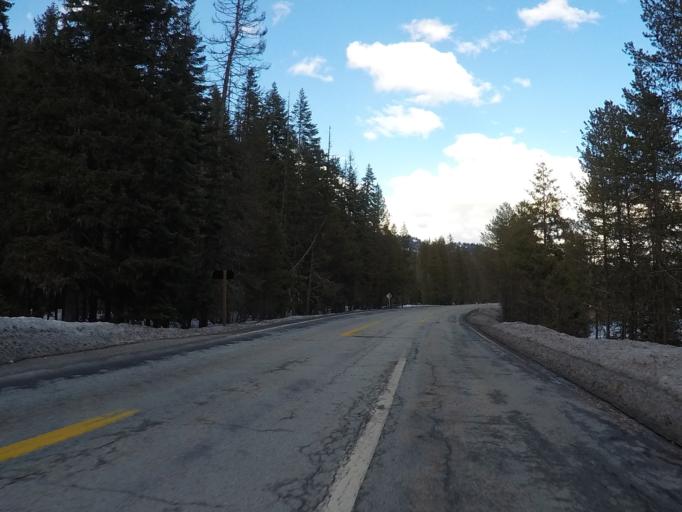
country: US
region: Montana
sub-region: Ravalli County
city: Hamilton
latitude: 46.5082
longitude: -114.7708
